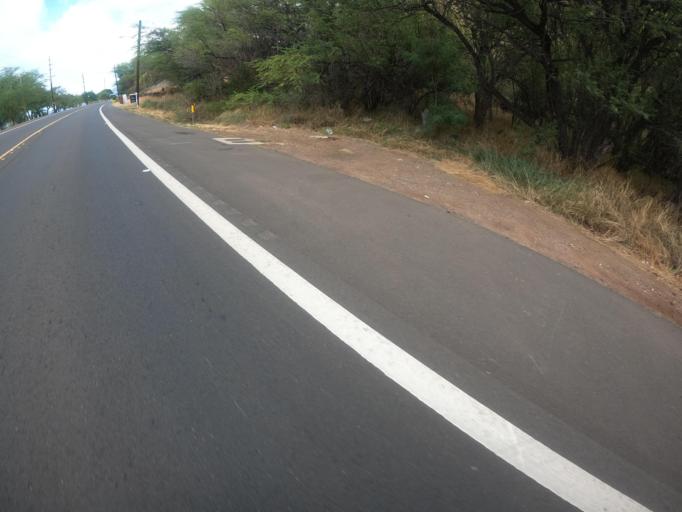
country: US
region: Hawaii
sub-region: Honolulu County
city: Makaha
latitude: 21.4838
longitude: -158.2281
